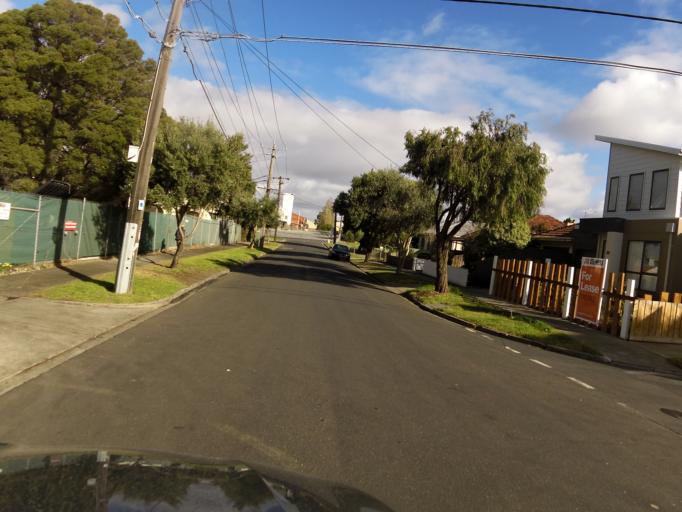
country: AU
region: Victoria
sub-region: Maribyrnong
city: West Footscray
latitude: -37.8031
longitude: 144.8630
